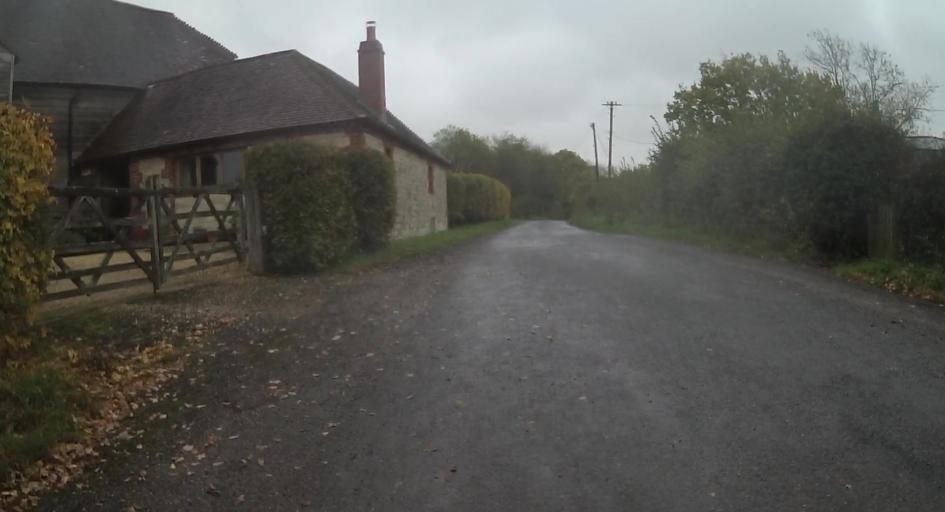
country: GB
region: England
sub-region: Surrey
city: Farnham
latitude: 51.2009
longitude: -0.8525
